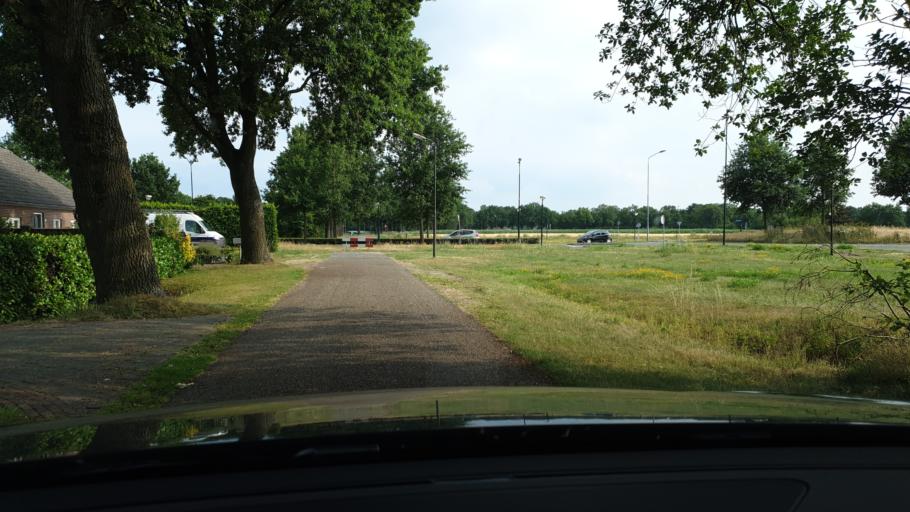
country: NL
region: North Brabant
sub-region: Gemeente Veldhoven
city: Oerle
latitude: 51.4351
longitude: 5.3778
